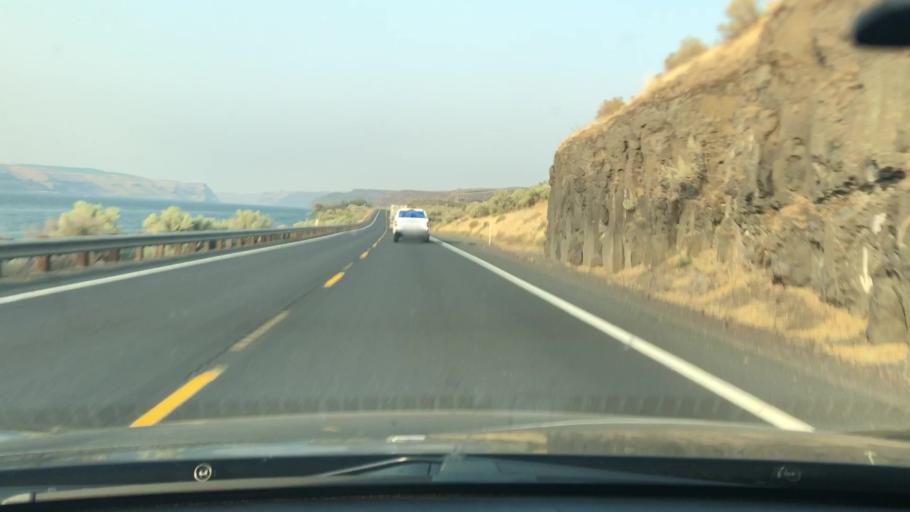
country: US
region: Oregon
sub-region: Umatilla County
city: Stanfield
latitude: 45.9237
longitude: -119.1128
